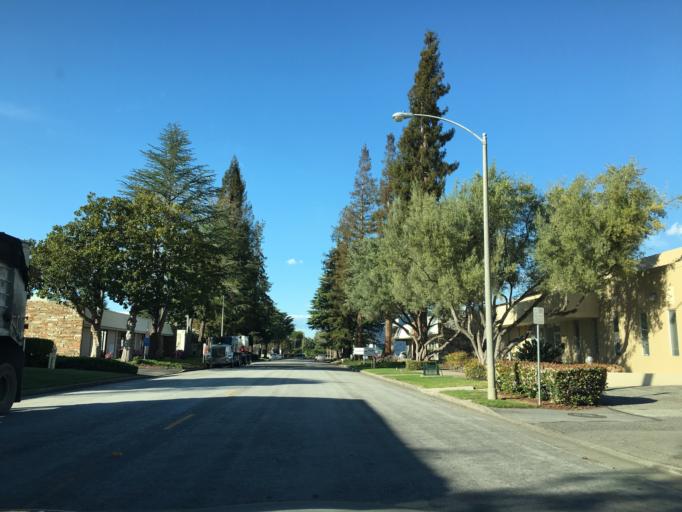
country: US
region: California
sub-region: Santa Clara County
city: Sunnyvale
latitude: 37.3957
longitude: -122.0327
